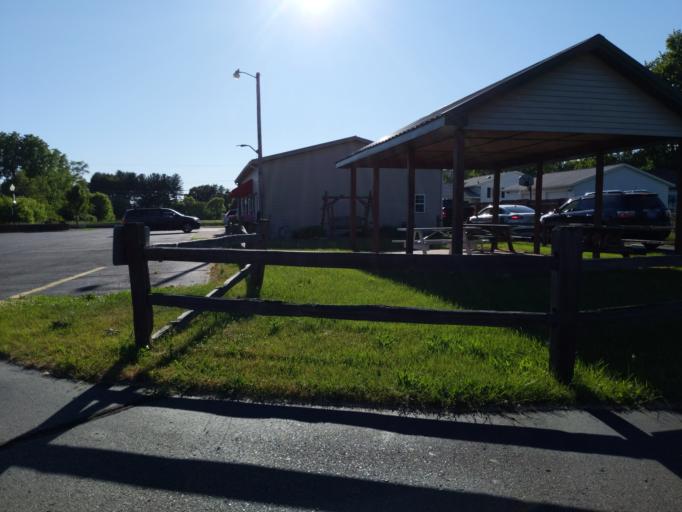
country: US
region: Michigan
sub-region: Ingham County
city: Stockbridge
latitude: 42.4423
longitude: -84.1791
